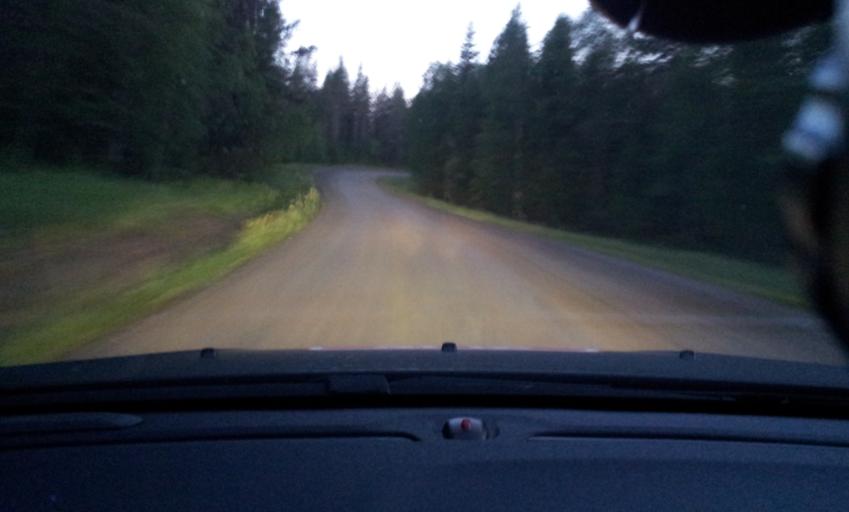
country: SE
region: Jaemtland
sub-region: Braecke Kommun
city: Braecke
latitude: 62.7261
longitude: 15.5041
